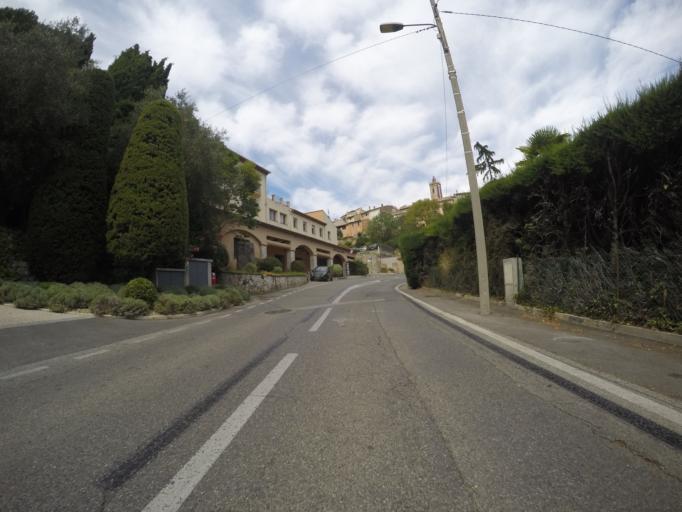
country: FR
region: Provence-Alpes-Cote d'Azur
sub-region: Departement des Alpes-Maritimes
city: Mougins
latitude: 43.5993
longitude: 6.9962
